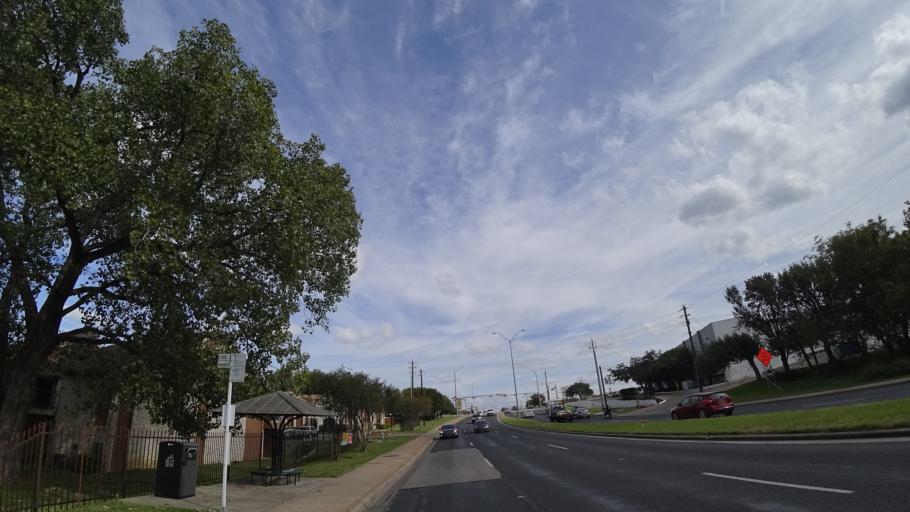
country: US
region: Texas
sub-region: Travis County
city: Onion Creek
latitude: 30.1918
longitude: -97.7743
